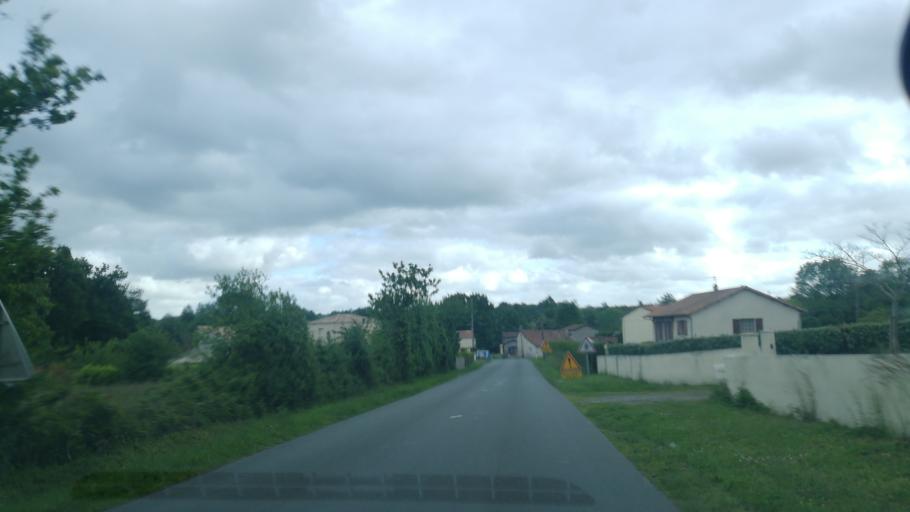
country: FR
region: Poitou-Charentes
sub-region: Departement des Deux-Sevres
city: La Chapelle-Saint-Laurent
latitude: 46.7514
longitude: -0.4935
